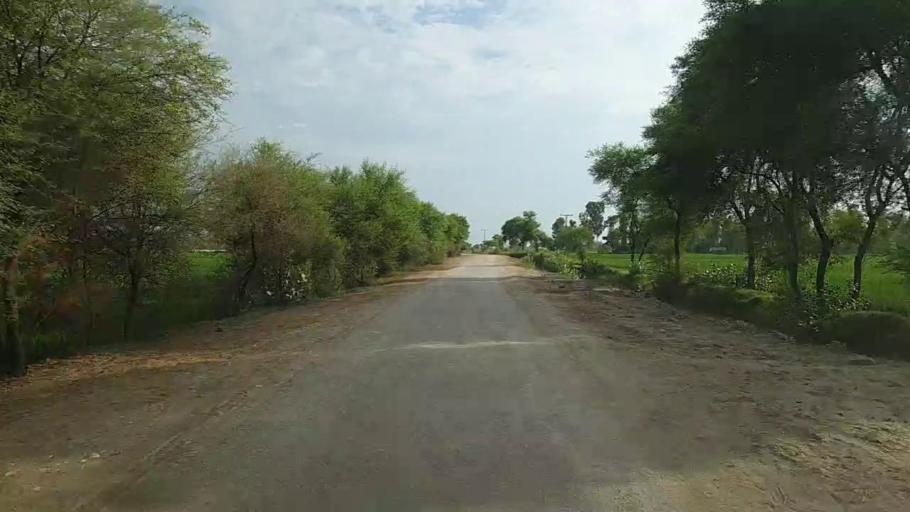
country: PK
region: Sindh
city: Thul
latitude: 28.2565
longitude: 68.8580
